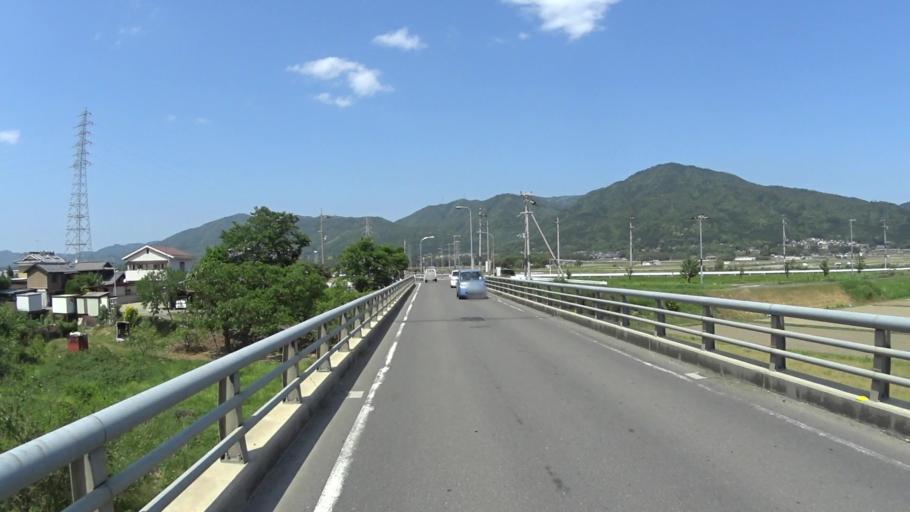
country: JP
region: Kyoto
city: Kameoka
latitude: 35.0279
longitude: 135.5717
